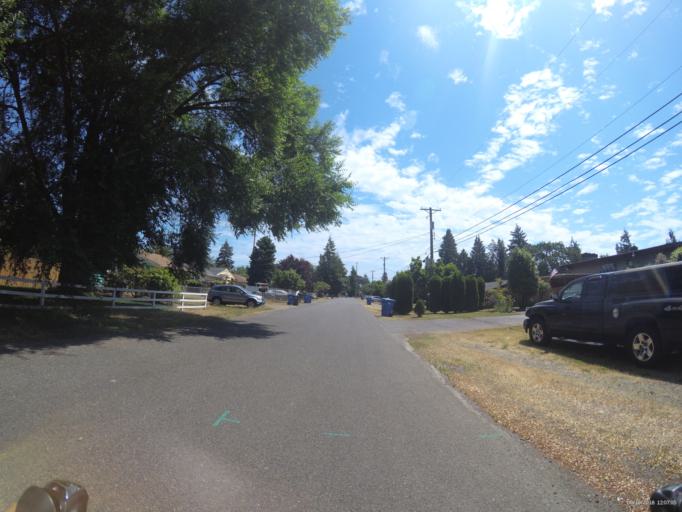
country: US
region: Washington
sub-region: Pierce County
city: Lakewood
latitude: 47.1768
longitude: -122.5326
